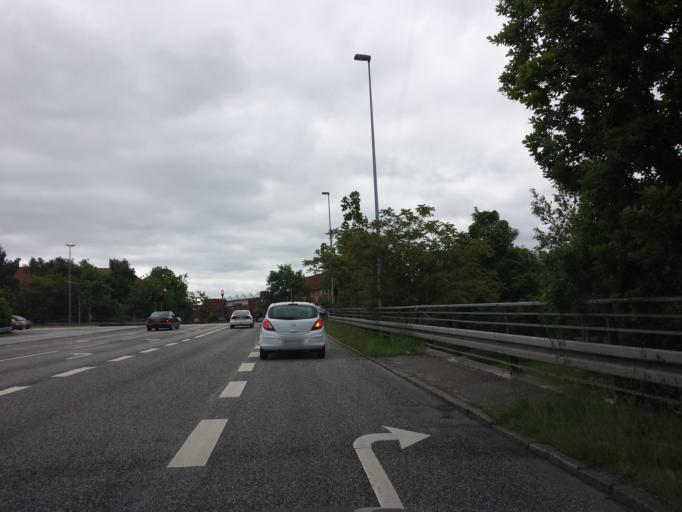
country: DK
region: Capital Region
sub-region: Ballerup Kommune
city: Ballerup
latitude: 55.7278
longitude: 12.3577
